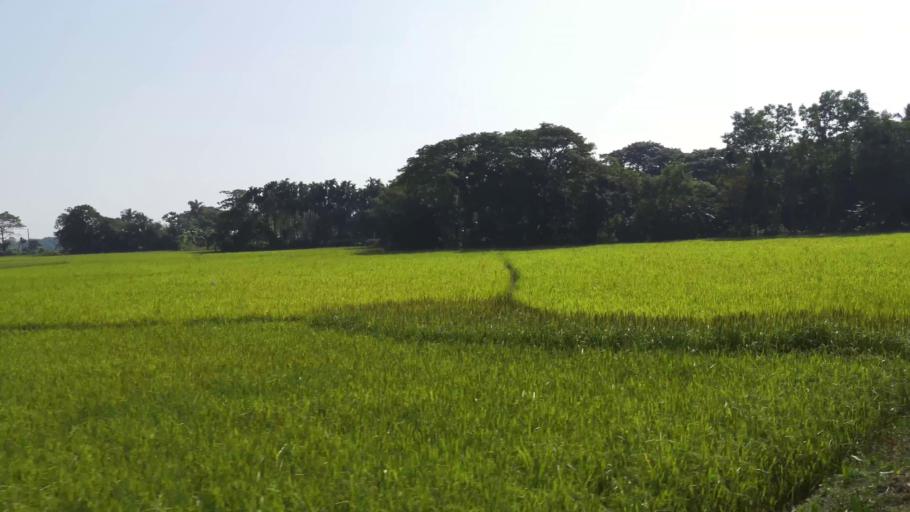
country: BD
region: Dhaka
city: Gafargaon
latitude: 24.5842
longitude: 90.5078
